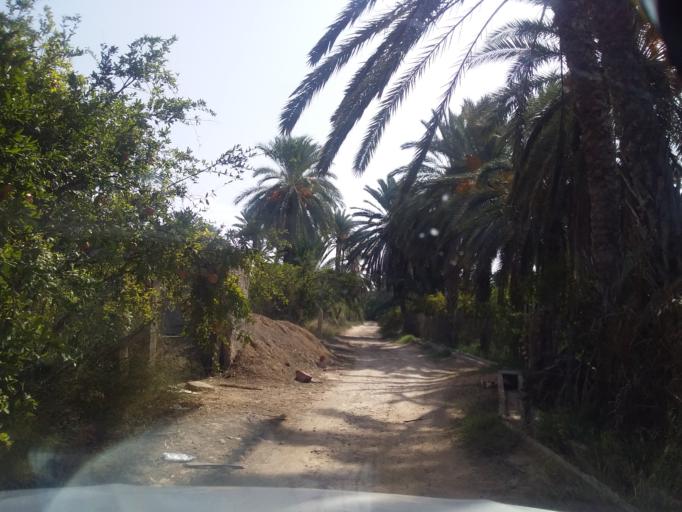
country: TN
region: Qabis
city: Gabes
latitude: 33.6275
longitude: 10.2891
